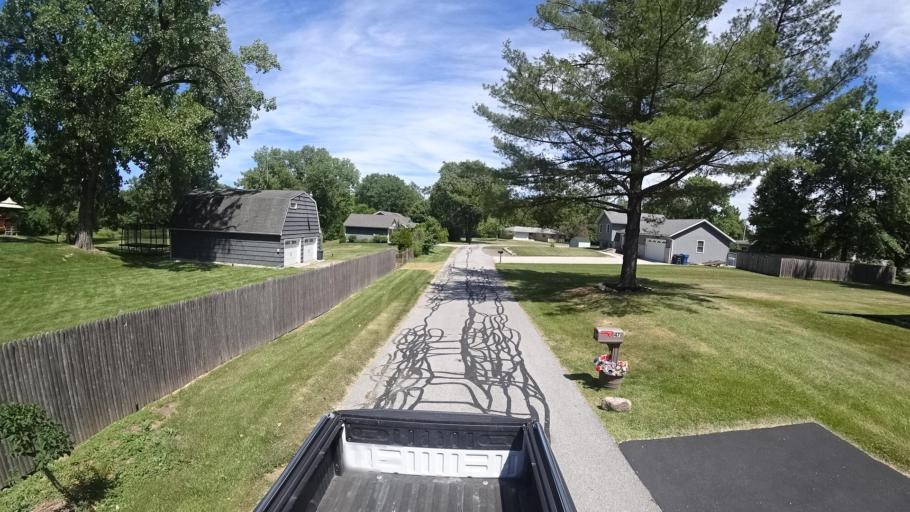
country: US
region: Indiana
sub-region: Porter County
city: Porter
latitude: 41.6210
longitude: -87.0668
